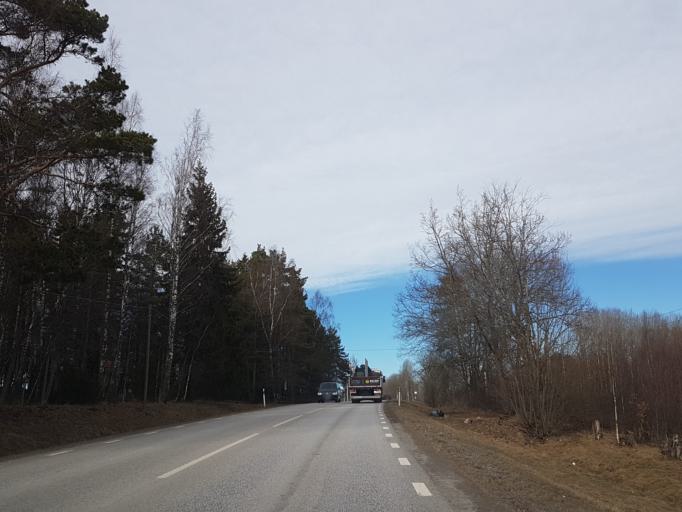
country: SE
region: Stockholm
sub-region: Norrtalje Kommun
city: Norrtalje
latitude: 59.7320
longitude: 18.6822
